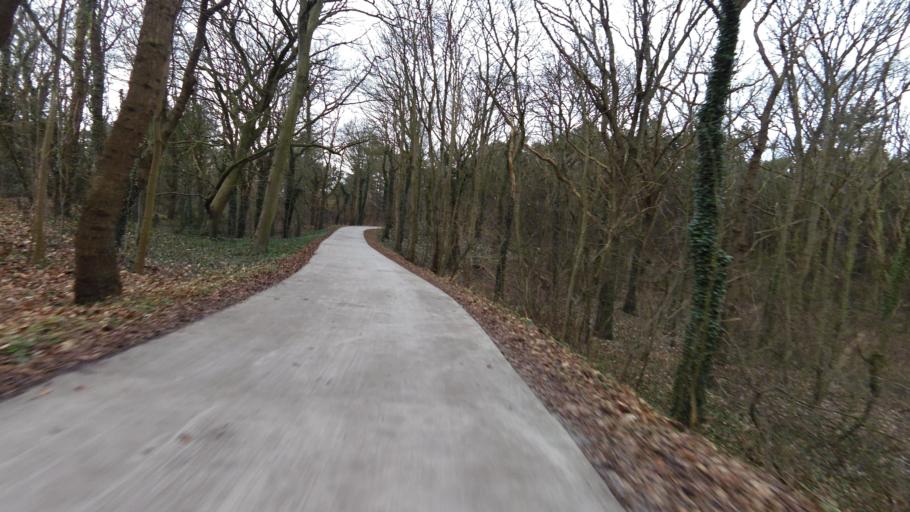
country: NL
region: North Holland
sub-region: Gemeente Heiloo
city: Heiloo
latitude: 52.6813
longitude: 4.6866
